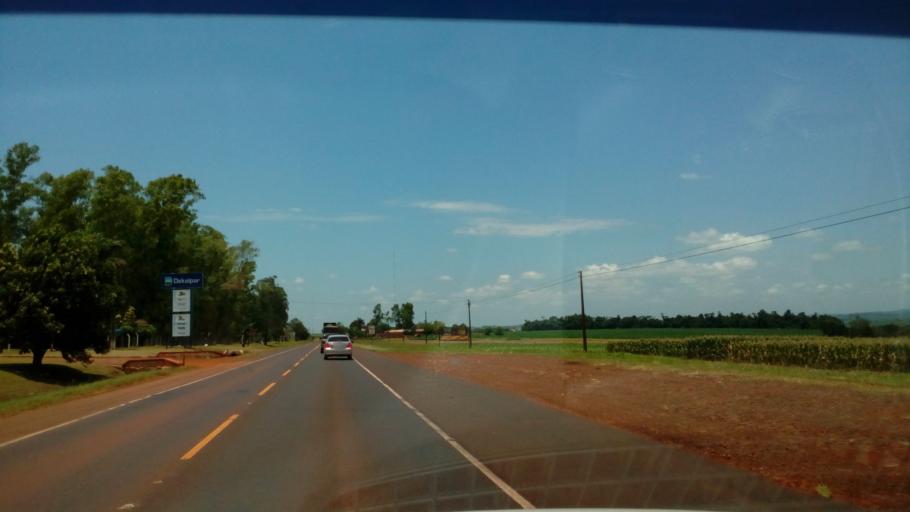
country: PY
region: Alto Parana
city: Santa Rita
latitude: -25.8636
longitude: -55.1177
